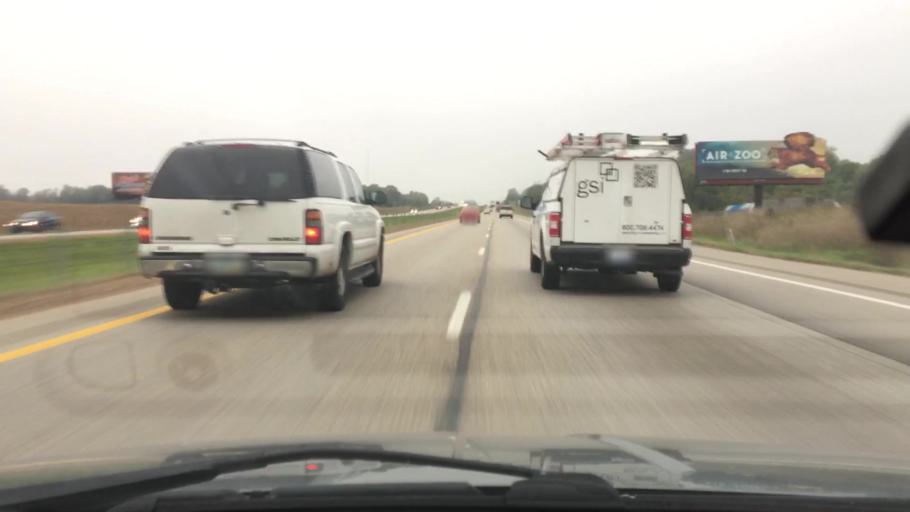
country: US
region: Michigan
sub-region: Calhoun County
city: Springfield
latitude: 42.2739
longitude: -85.3022
